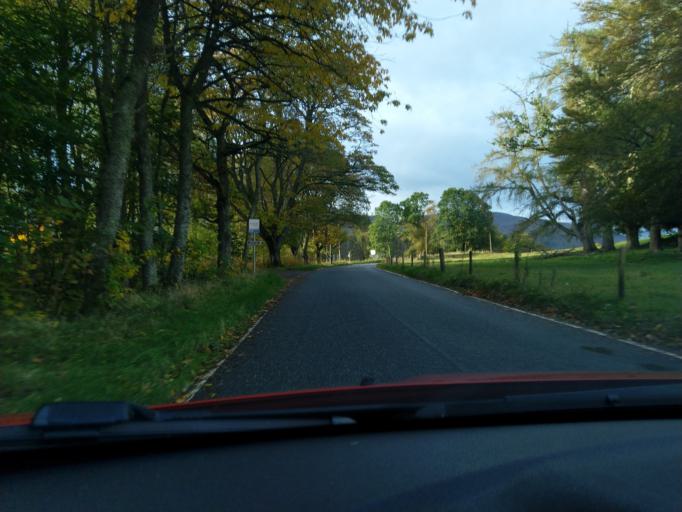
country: GB
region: Scotland
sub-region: Perth and Kinross
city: Aberfeldy
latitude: 56.7046
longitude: -4.1258
